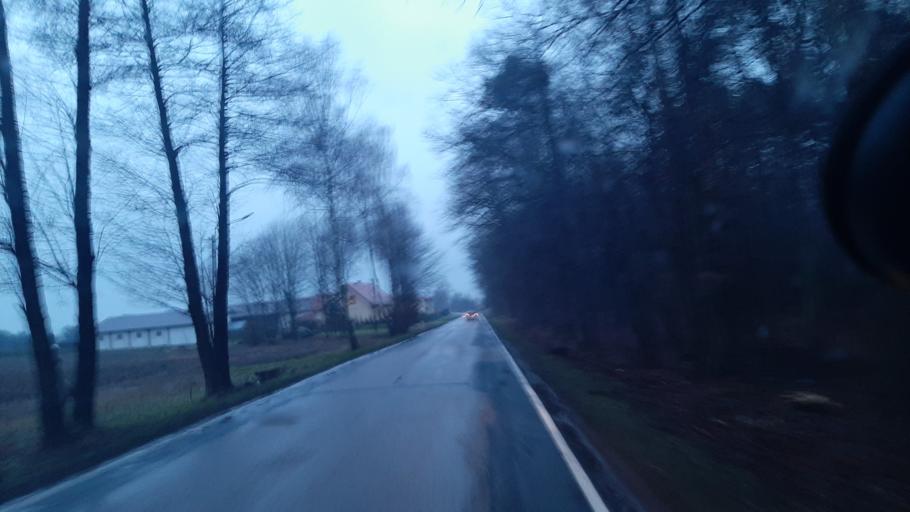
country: PL
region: Lublin Voivodeship
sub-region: Powiat lubartowski
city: Kamionka
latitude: 51.4215
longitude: 22.4191
